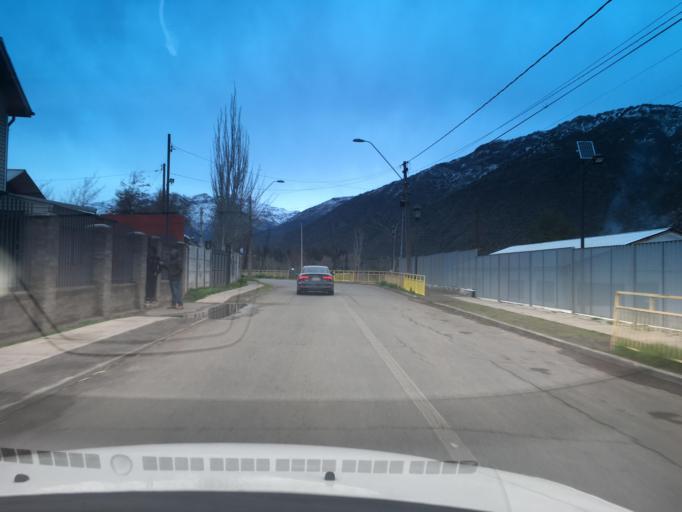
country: CL
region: Santiago Metropolitan
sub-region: Provincia de Cordillera
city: Puente Alto
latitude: -33.6435
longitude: -70.3547
